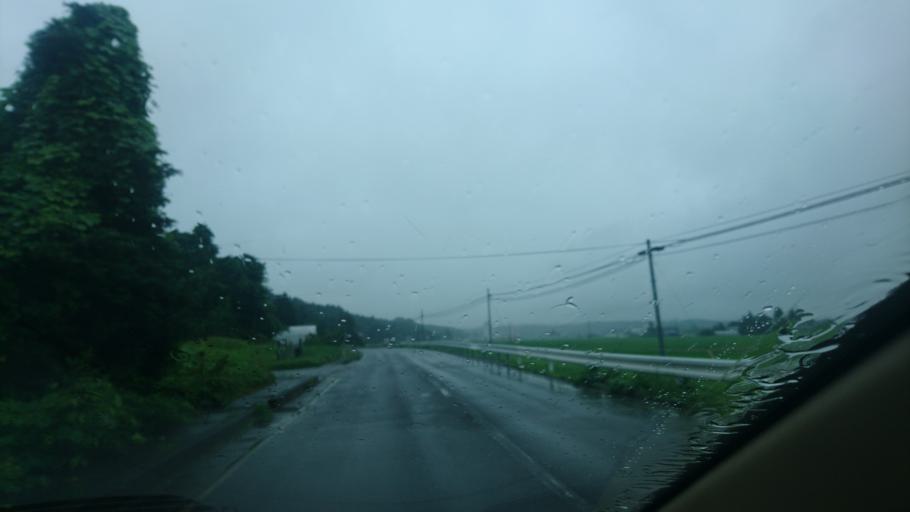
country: JP
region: Iwate
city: Kitakami
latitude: 39.2180
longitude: 141.1425
